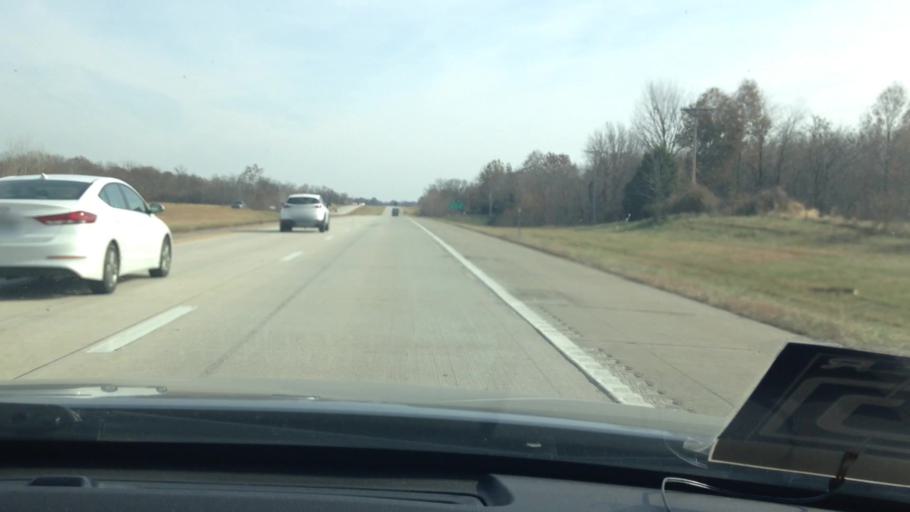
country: US
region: Missouri
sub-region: Cass County
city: Garden City
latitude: 38.4639
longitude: -93.9911
